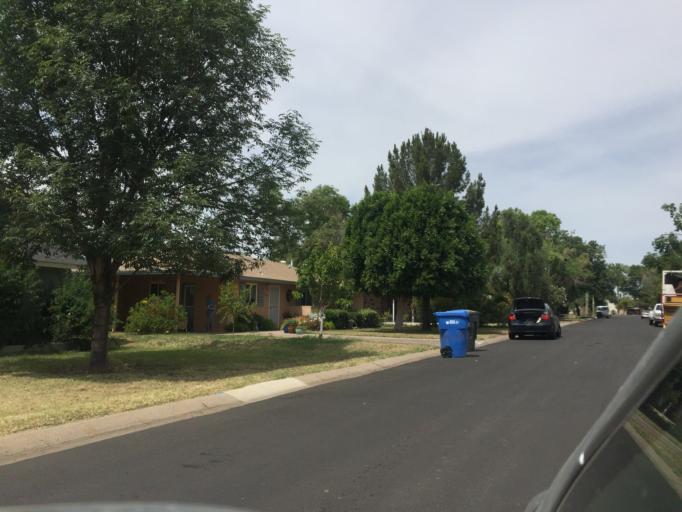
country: US
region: Arizona
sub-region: Maricopa County
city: Phoenix
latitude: 33.5293
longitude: -112.0524
